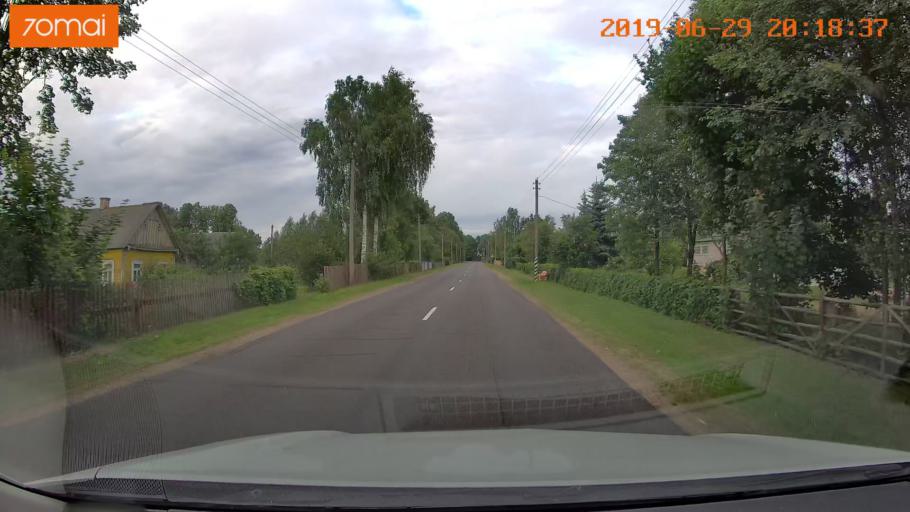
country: BY
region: Brest
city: Asnyezhytsy
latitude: 52.3953
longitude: 26.2376
